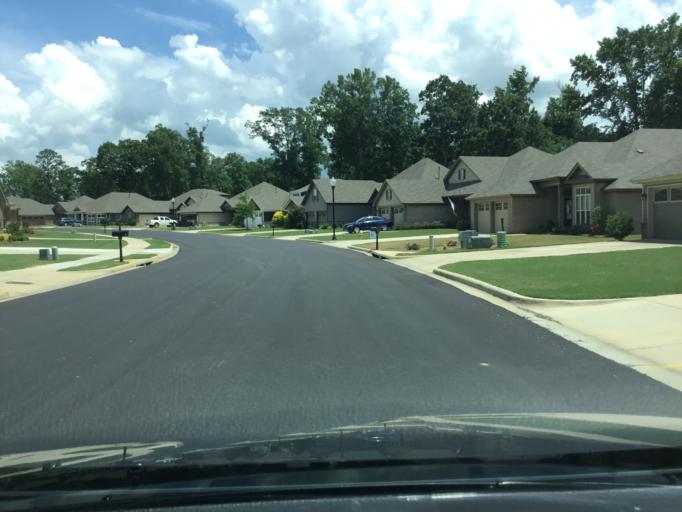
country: US
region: Alabama
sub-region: Montgomery County
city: Pike Road
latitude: 32.3368
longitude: -86.0798
